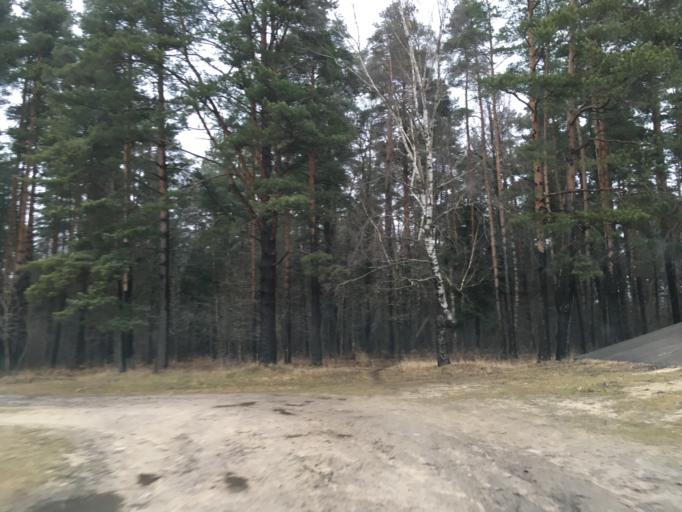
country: LV
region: Ozolnieku
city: Ozolnieki
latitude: 56.6927
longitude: 23.7854
